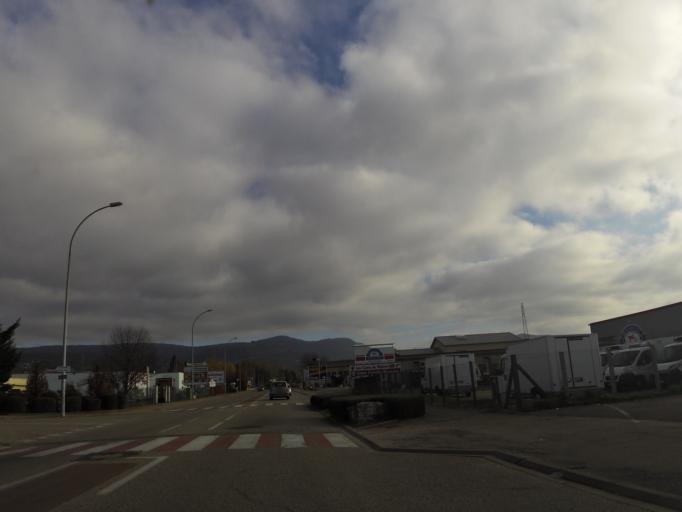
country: FR
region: Rhone-Alpes
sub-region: Departement de l'Ain
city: Amberieu-en-Bugey
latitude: 45.9637
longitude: 5.3416
